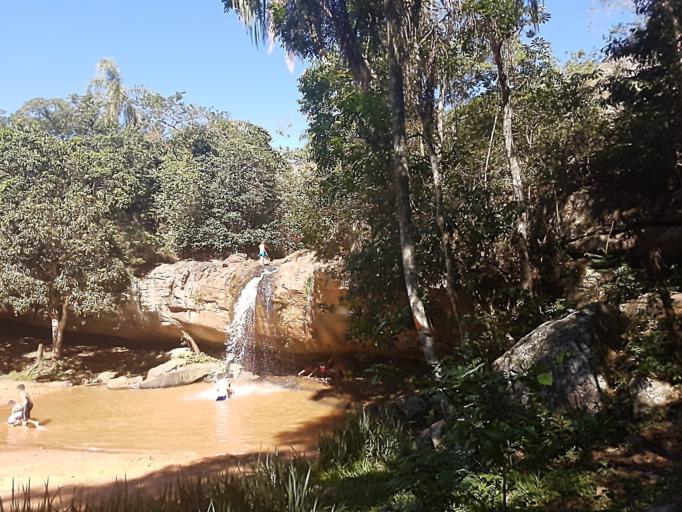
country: PY
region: Cordillera
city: Atyra
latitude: -25.2704
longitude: -57.1286
